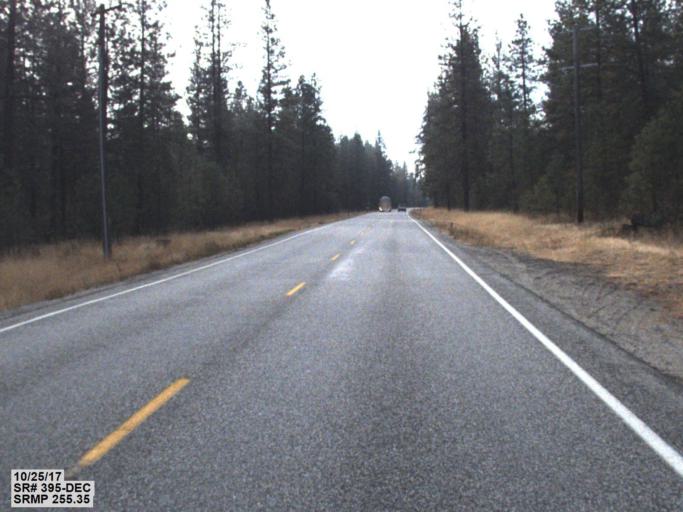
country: US
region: Washington
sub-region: Stevens County
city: Kettle Falls
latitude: 48.8065
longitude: -118.1633
